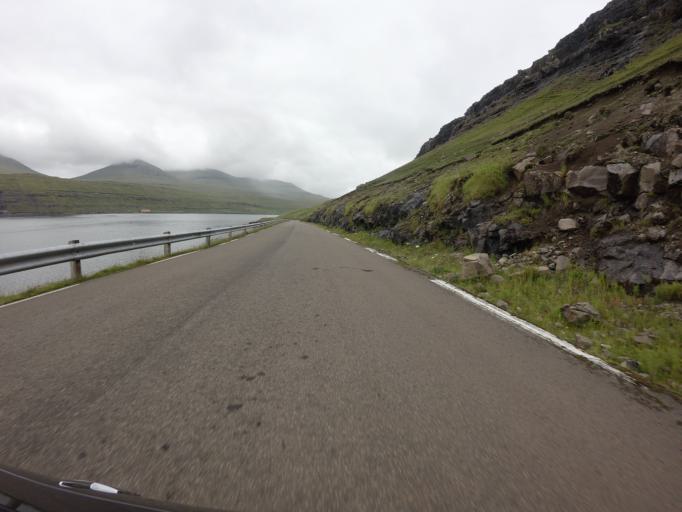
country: FO
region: Eysturoy
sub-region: Eidi
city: Eidi
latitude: 62.2836
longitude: -7.1004
